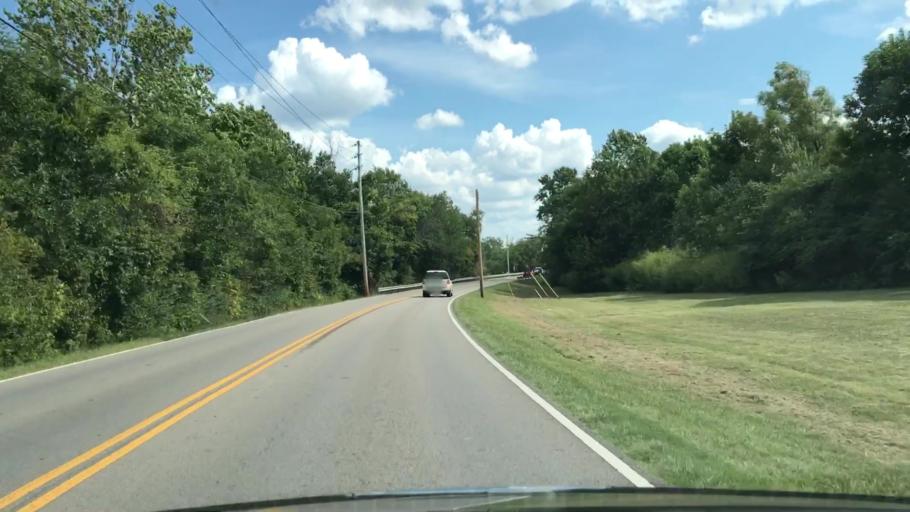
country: US
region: Tennessee
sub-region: Maury County
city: Spring Hill
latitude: 35.7423
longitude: -86.9258
